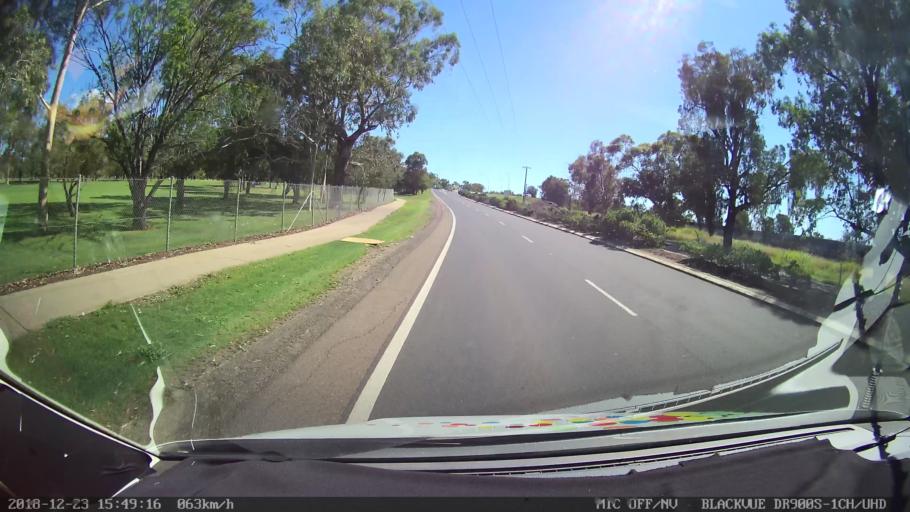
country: AU
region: New South Wales
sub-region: Tamworth Municipality
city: South Tamworth
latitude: -31.0980
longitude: 150.9078
